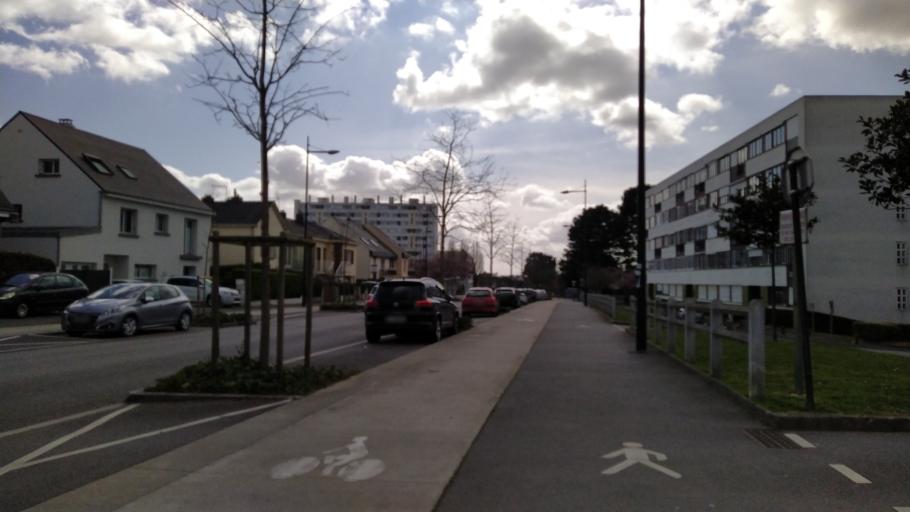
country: FR
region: Pays de la Loire
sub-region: Departement de la Loire-Atlantique
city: Orvault
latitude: 47.2431
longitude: -1.6075
